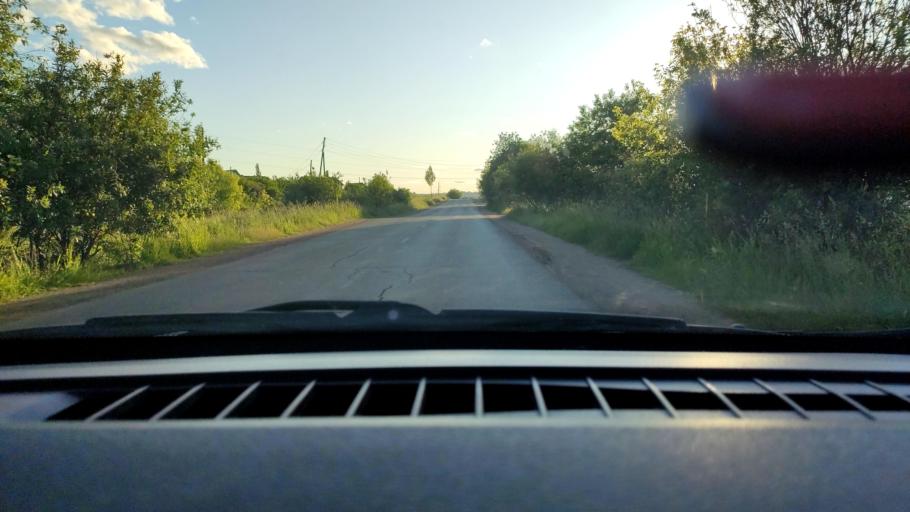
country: RU
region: Perm
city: Kultayevo
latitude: 57.9284
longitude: 55.8708
